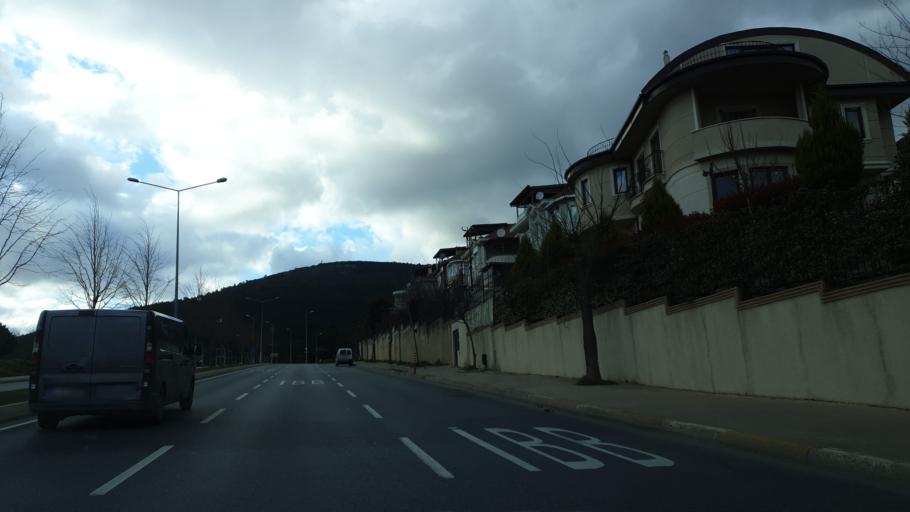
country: TR
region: Istanbul
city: Sultanbeyli
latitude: 40.9225
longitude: 29.2675
